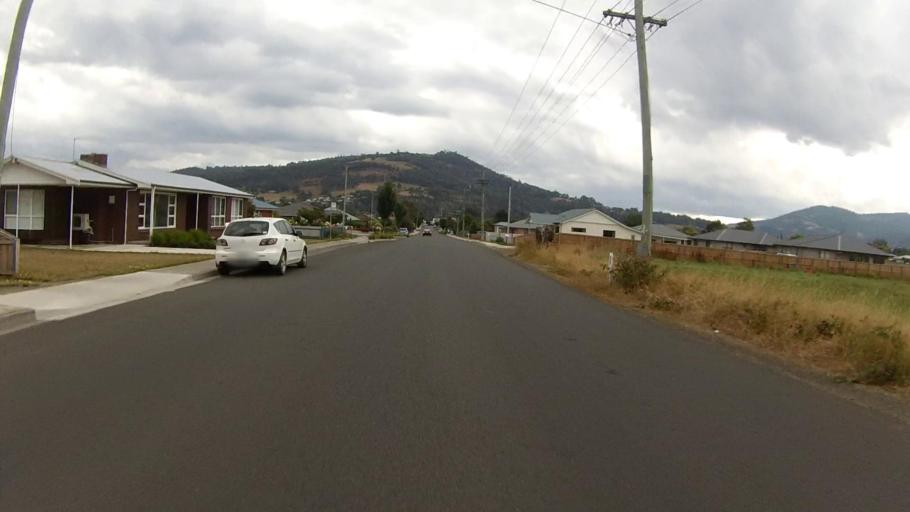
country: AU
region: Tasmania
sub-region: Huon Valley
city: Huonville
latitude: -43.0289
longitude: 147.0578
